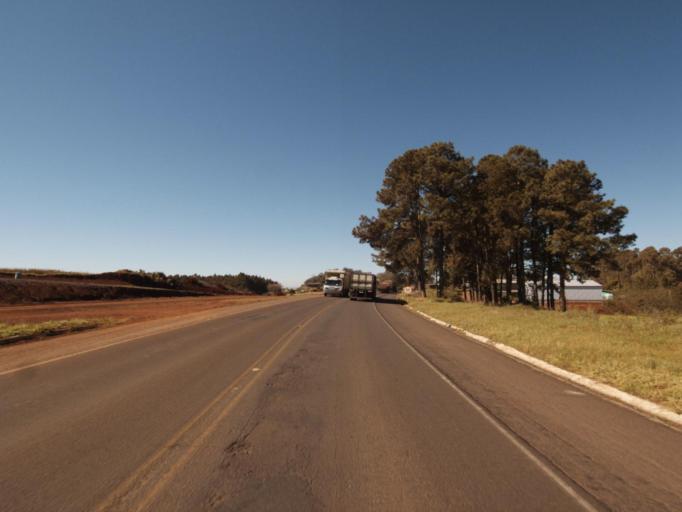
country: BR
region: Santa Catarina
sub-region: Chapeco
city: Chapeco
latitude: -26.8795
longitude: -52.9482
